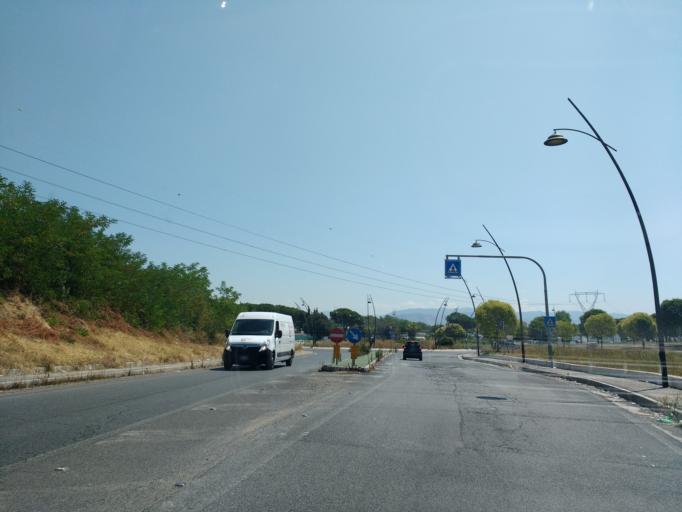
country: IT
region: Latium
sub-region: Citta metropolitana di Roma Capitale
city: Setteville
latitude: 41.9471
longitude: 12.6709
